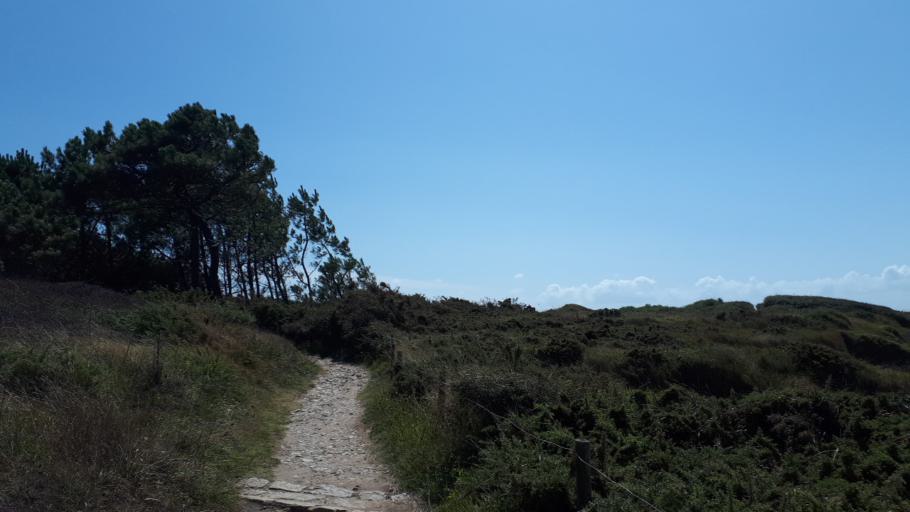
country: FR
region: Brittany
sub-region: Departement du Morbihan
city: Penestin
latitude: 47.4892
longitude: -2.5009
